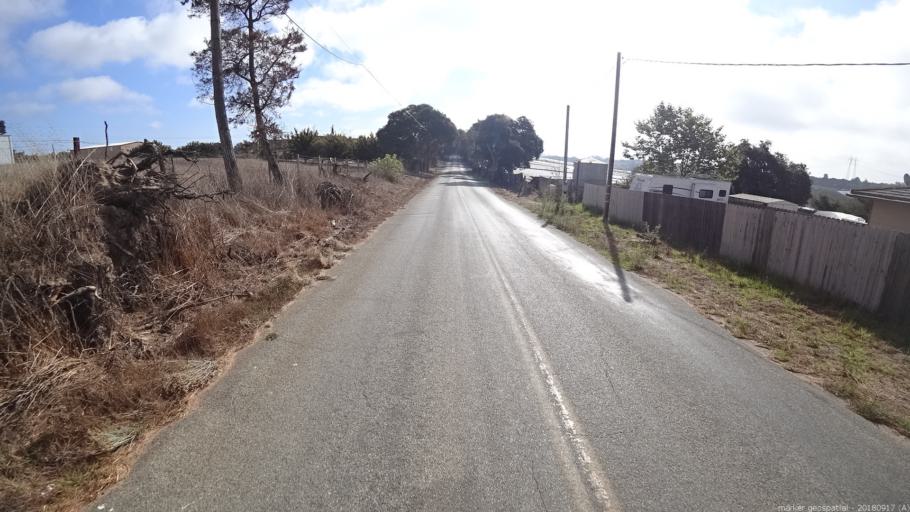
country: US
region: California
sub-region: Monterey County
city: Elkhorn
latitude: 36.7894
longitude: -121.7135
